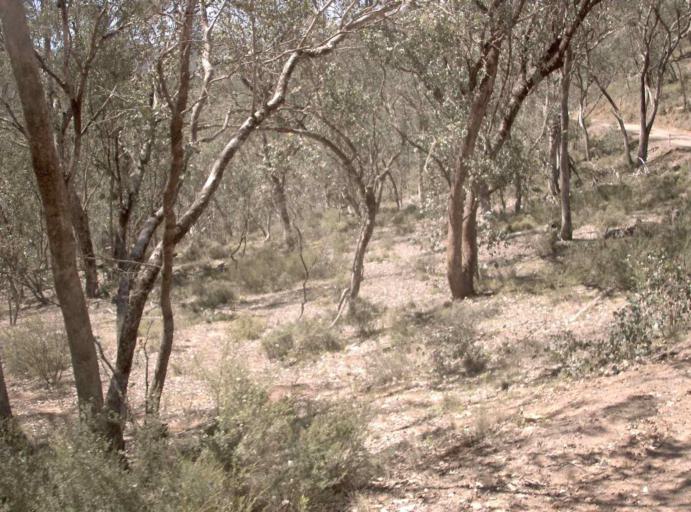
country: AU
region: New South Wales
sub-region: Snowy River
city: Jindabyne
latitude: -37.0509
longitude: 148.5380
